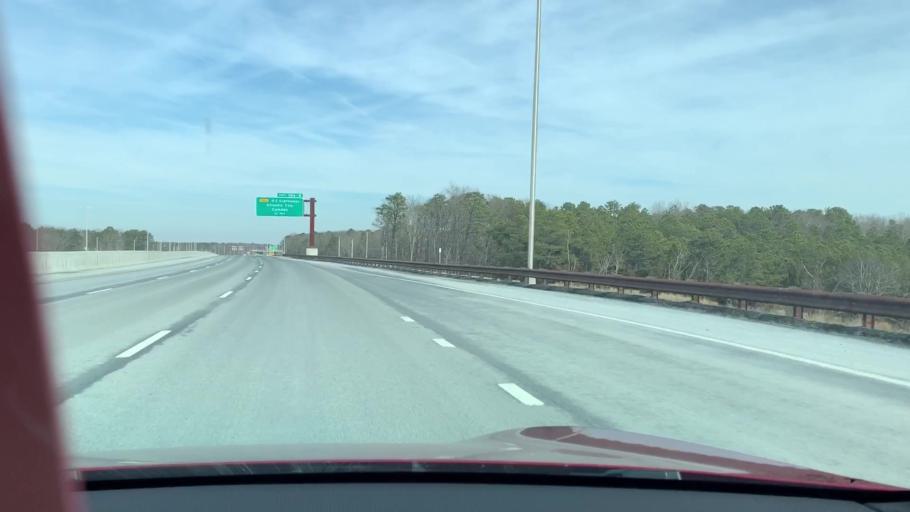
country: US
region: New Jersey
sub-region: Atlantic County
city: Northfield
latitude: 39.4030
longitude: -74.5578
